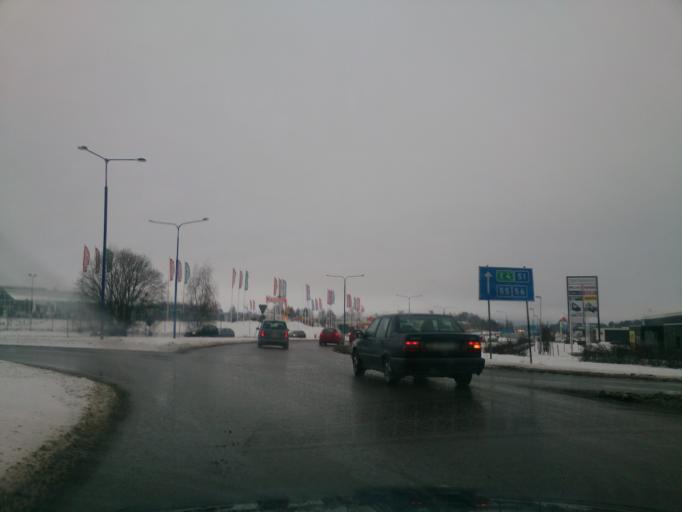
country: SE
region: OEstergoetland
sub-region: Norrkopings Kommun
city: Norrkoping
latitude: 58.6092
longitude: 16.1611
